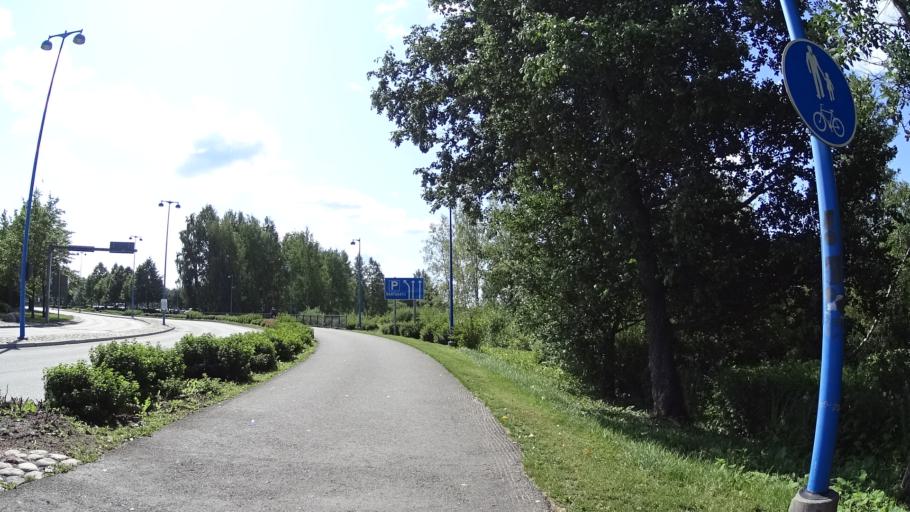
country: FI
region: Uusimaa
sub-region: Helsinki
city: Jaervenpaeae
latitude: 60.4709
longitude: 25.0813
